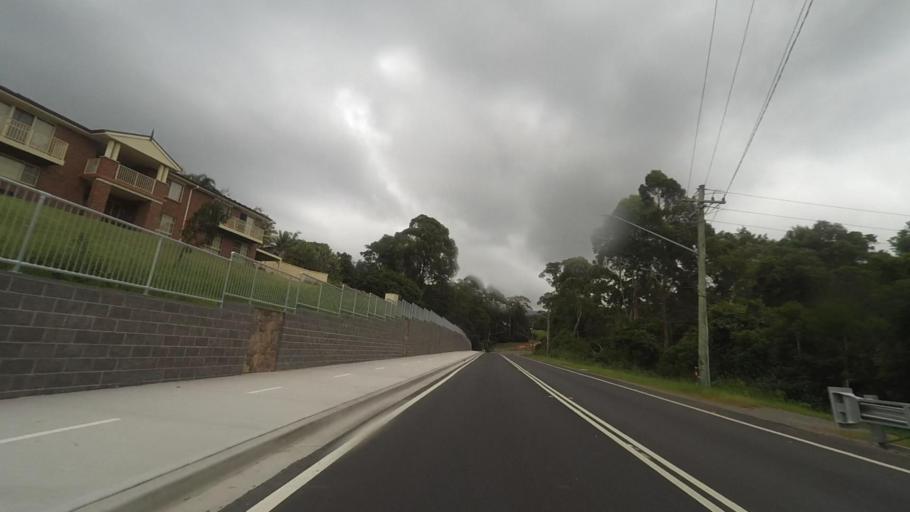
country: AU
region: New South Wales
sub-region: Wollongong
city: Cordeaux Heights
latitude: -34.4390
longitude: 150.8376
